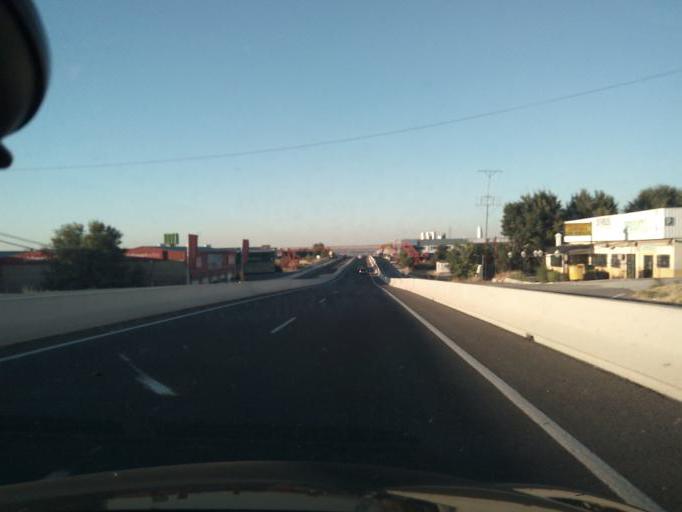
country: ES
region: Madrid
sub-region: Provincia de Madrid
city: Ajalvir
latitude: 40.5162
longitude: -3.4809
